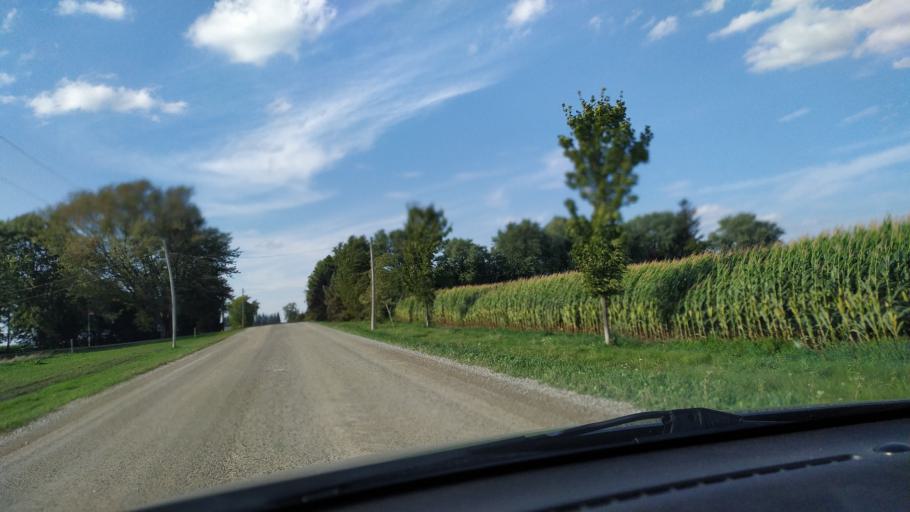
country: CA
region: Ontario
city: Stratford
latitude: 43.2710
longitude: -80.9401
